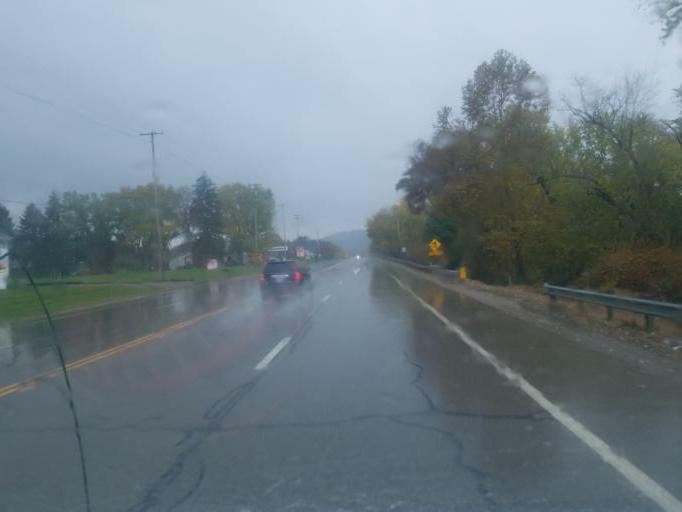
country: US
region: Ohio
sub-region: Muskingum County
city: South Zanesville
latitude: 39.9100
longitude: -82.0014
